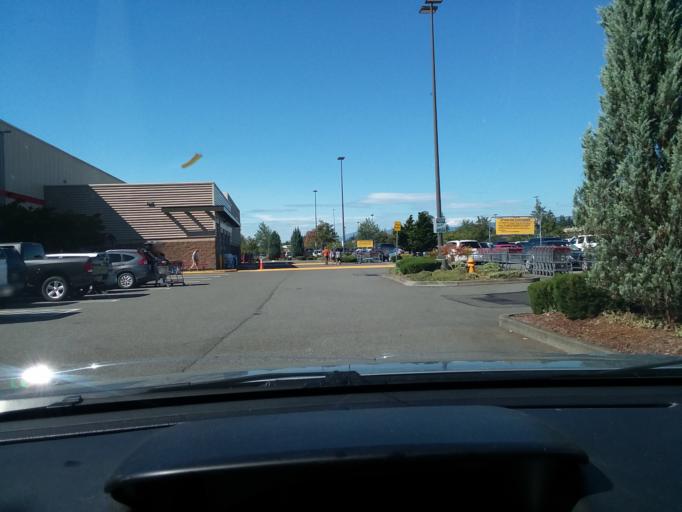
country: US
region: Washington
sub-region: Snohomish County
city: Smokey Point
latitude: 48.1470
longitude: -122.1908
